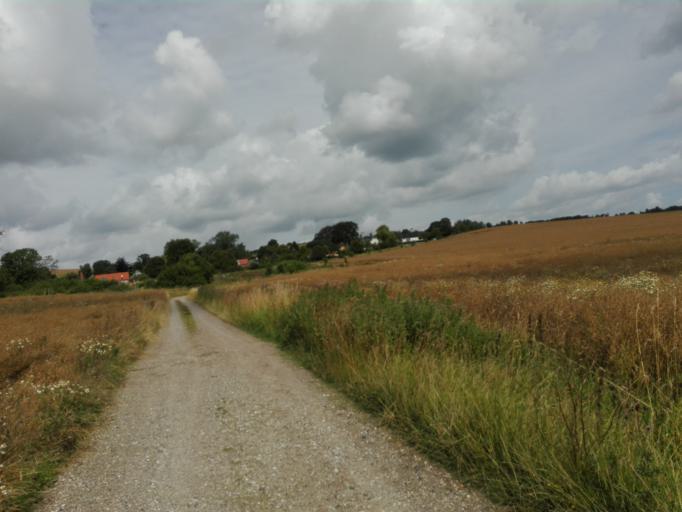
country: DK
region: Central Jutland
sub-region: Arhus Kommune
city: Marslet
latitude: 56.0809
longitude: 10.1821
